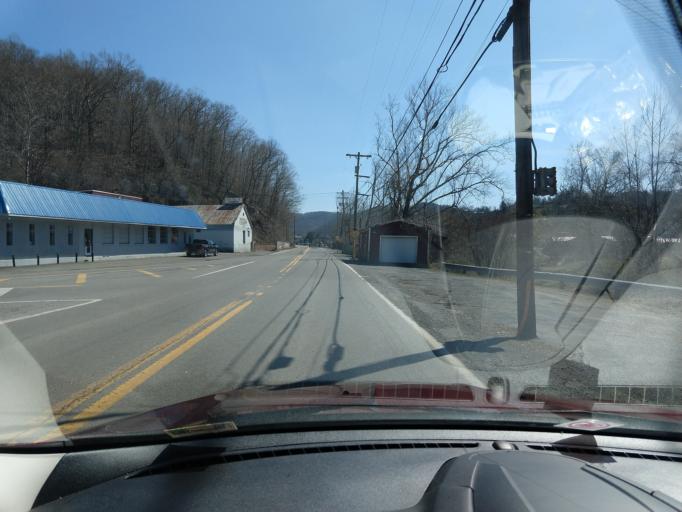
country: US
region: West Virginia
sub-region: Braxton County
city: Sutton
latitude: 38.6672
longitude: -80.7168
